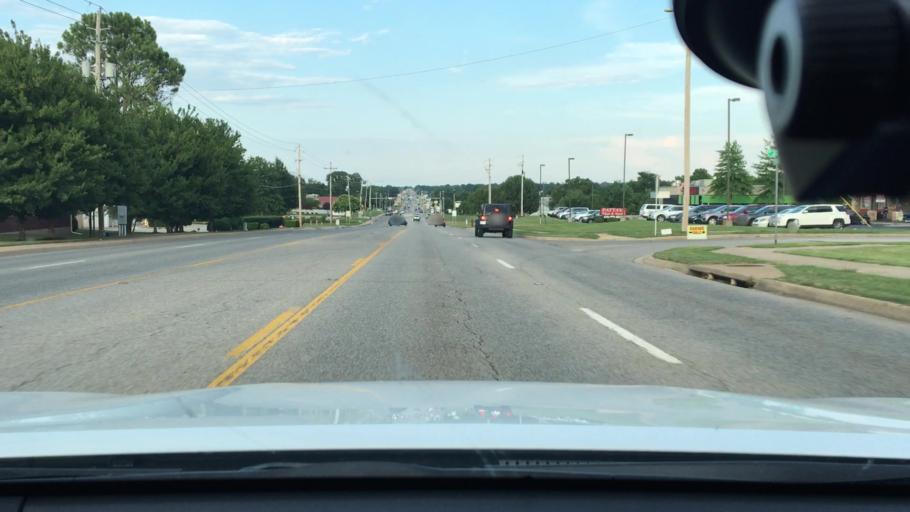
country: US
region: Arkansas
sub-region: Benton County
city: Rogers
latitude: 36.3346
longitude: -94.1698
